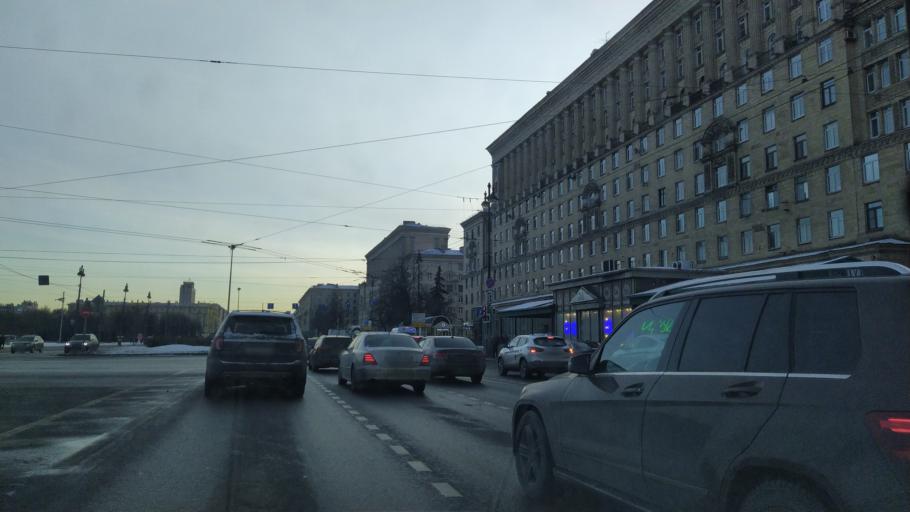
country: RU
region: St.-Petersburg
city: Kupchino
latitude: 59.8536
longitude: 30.3208
